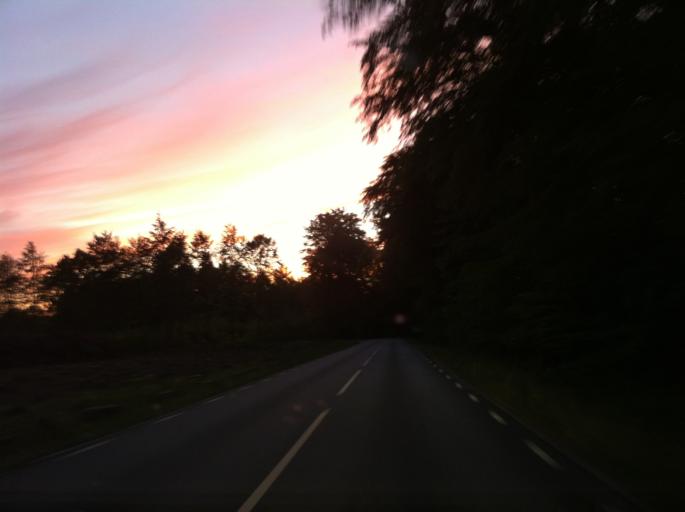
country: SE
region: Skane
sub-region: Tomelilla Kommun
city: Tomelilla
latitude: 55.5552
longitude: 13.9324
